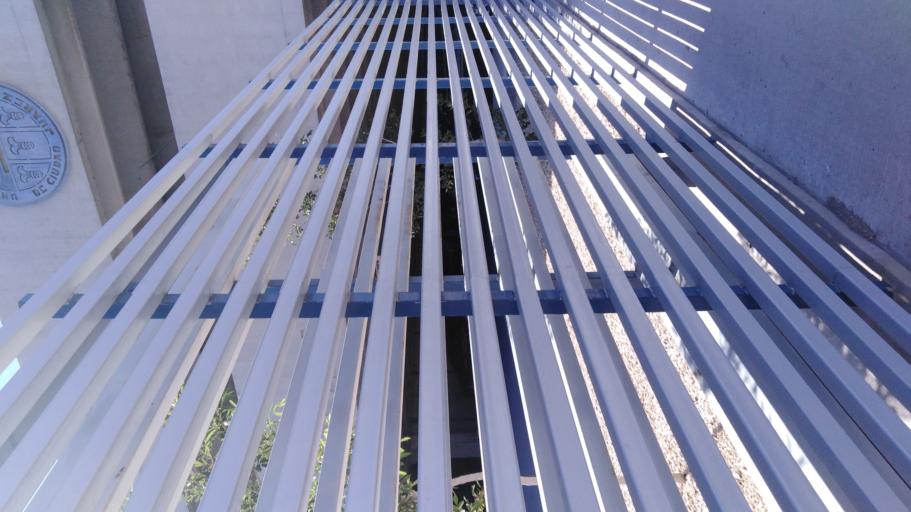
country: MX
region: Chihuahua
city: Ciudad Juarez
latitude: 31.7423
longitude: -106.4346
